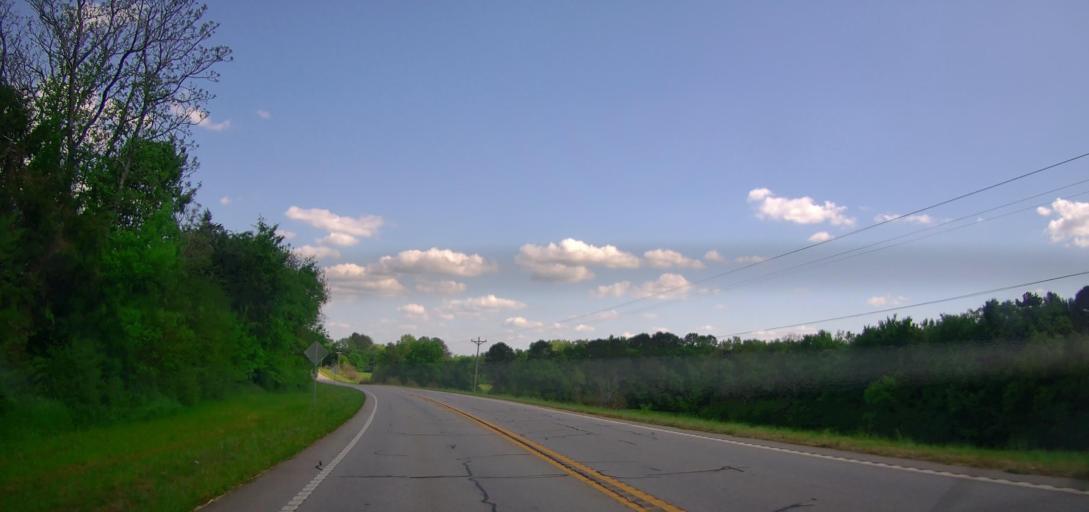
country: US
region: Georgia
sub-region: Greene County
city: Greensboro
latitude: 33.5995
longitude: -83.3048
